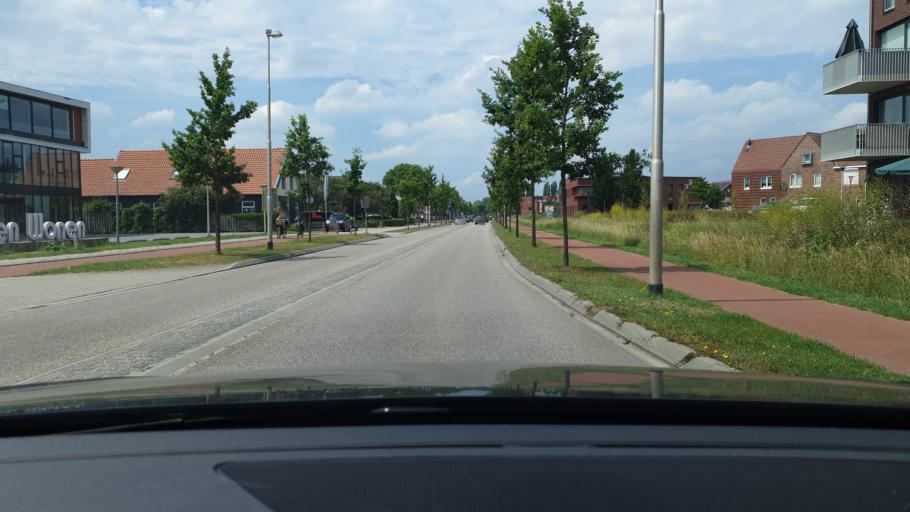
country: NL
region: Gelderland
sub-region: Gemeente Overbetuwe
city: Elst
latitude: 51.9153
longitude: 5.8666
